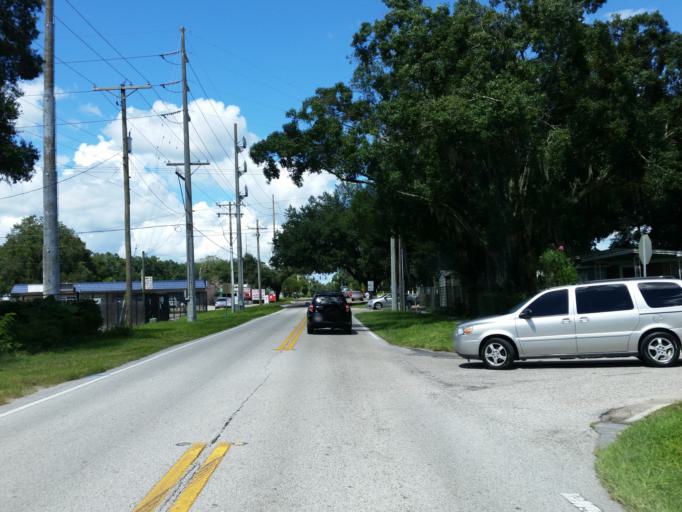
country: US
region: Florida
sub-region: Hillsborough County
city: Brandon
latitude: 27.9355
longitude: -82.2776
